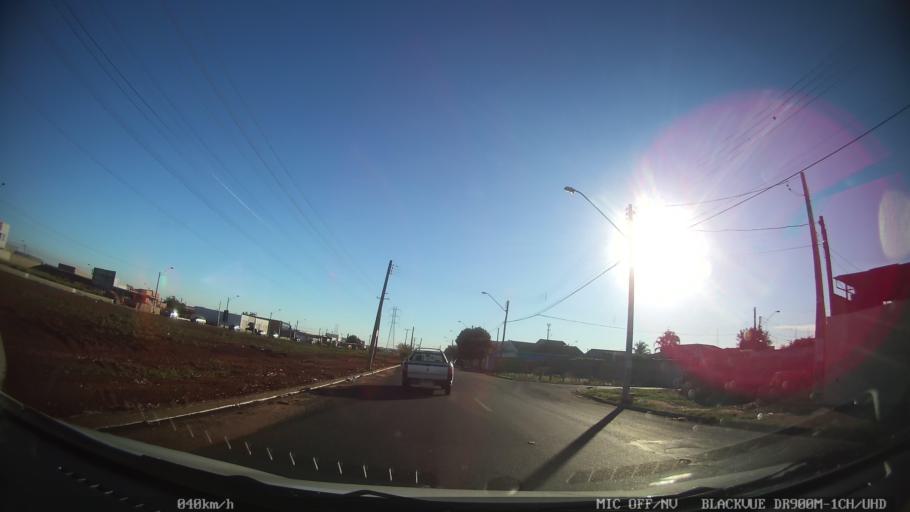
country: BR
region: Sao Paulo
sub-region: Americo Brasiliense
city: Americo Brasiliense
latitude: -21.7469
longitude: -48.1459
